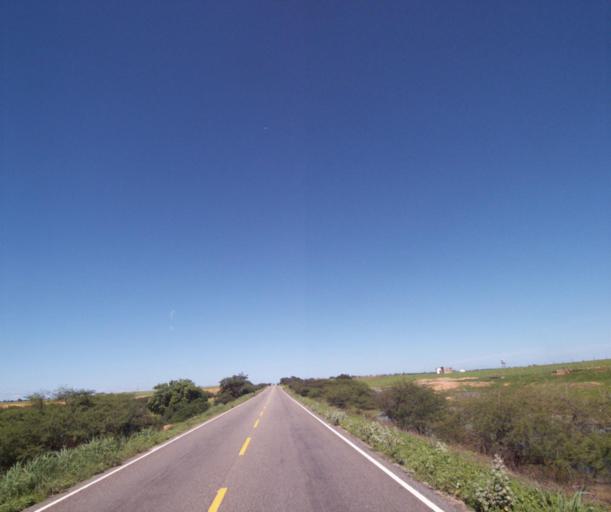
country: BR
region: Bahia
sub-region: Palmas De Monte Alto
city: Palmas de Monte Alto
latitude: -14.2544
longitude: -43.2230
